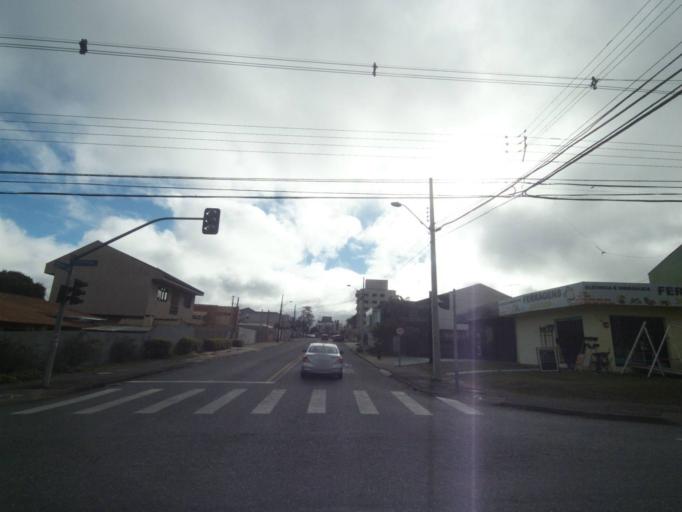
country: BR
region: Parana
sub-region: Sao Jose Dos Pinhais
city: Sao Jose dos Pinhais
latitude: -25.5226
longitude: -49.2999
